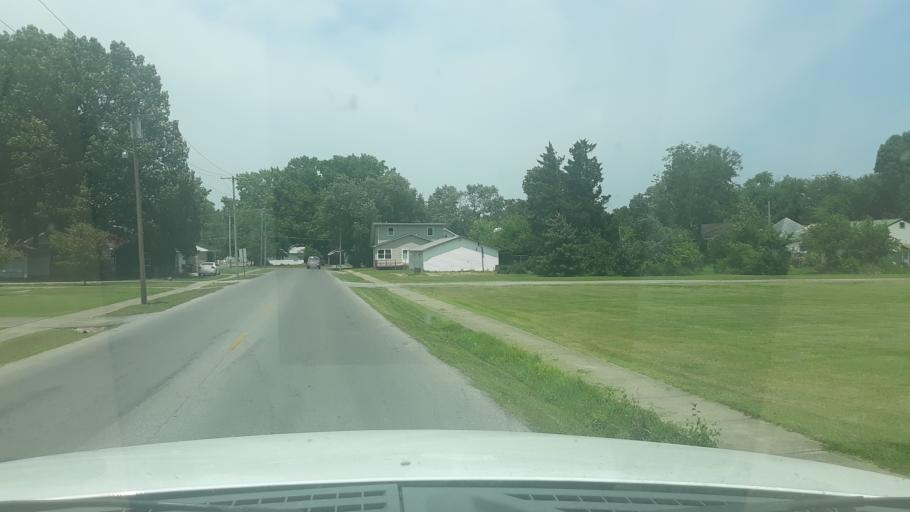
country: US
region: Illinois
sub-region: Saline County
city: Harrisburg
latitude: 37.7301
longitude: -88.5527
